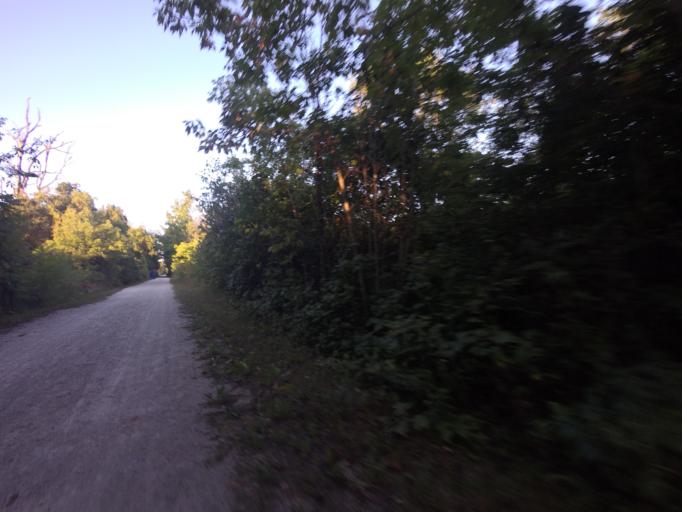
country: CA
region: Ontario
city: Brampton
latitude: 43.8814
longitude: -79.8492
